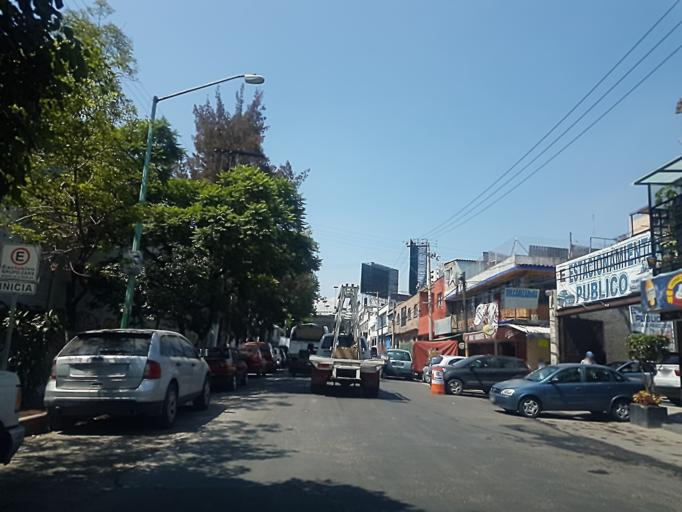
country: MX
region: Mexico
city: Naucalpan de Juarez
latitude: 19.4685
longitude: -99.2244
